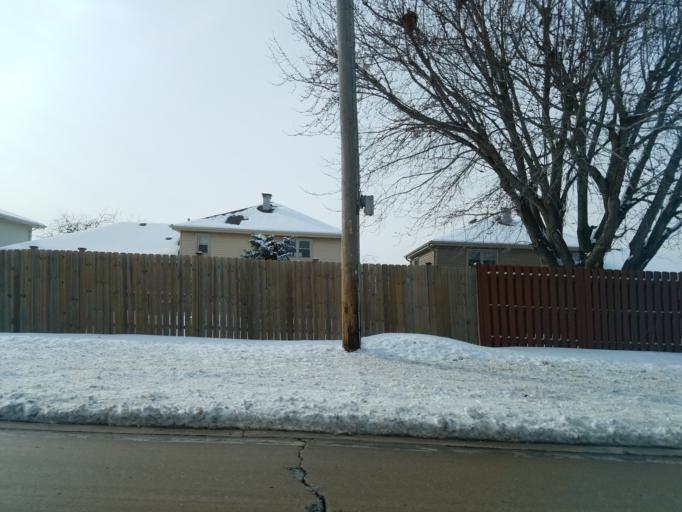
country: US
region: Illinois
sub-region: Cook County
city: Orland Hills
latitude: 41.5934
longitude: -87.8135
